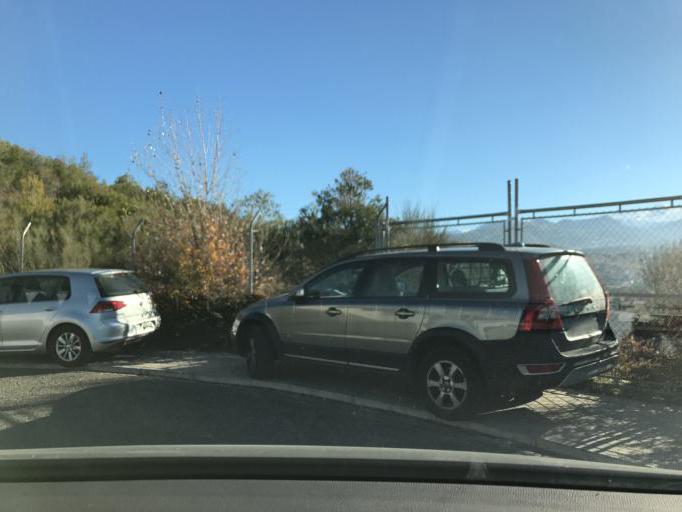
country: ES
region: Andalusia
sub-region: Provincia de Granada
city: Huetor Vega
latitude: 37.1586
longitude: -3.5727
